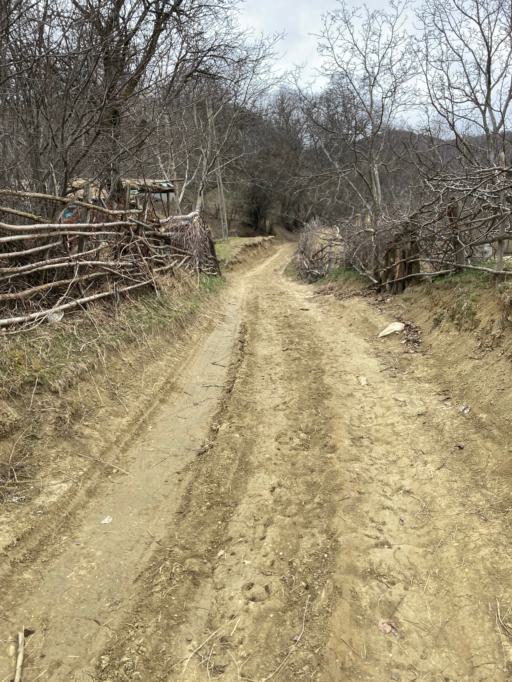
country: RO
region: Buzau
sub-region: Comuna Bozioru
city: Bozioru
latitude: 45.3695
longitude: 26.4680
